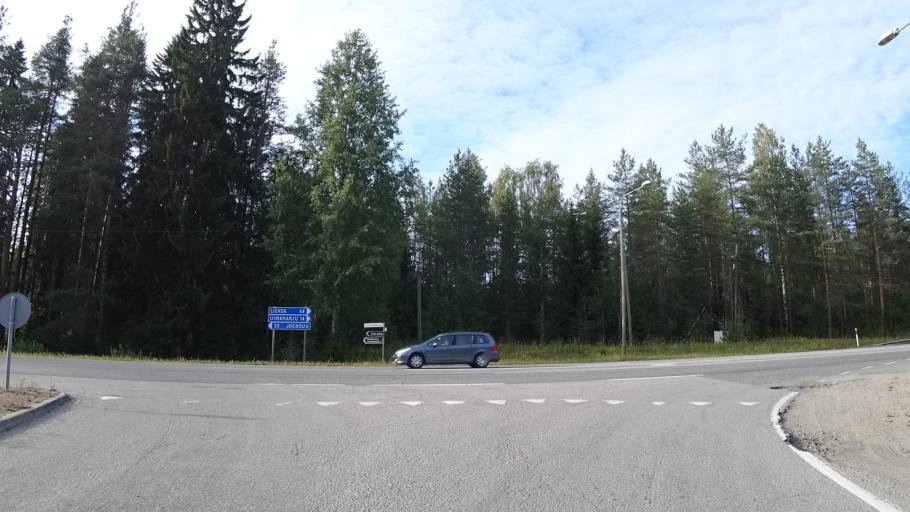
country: FI
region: North Karelia
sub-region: Joensuu
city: Eno
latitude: 62.8082
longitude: 30.1509
